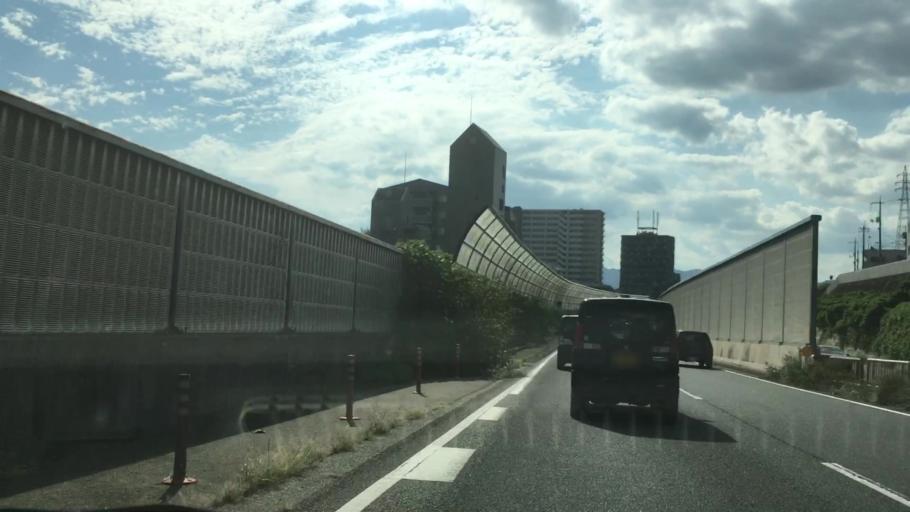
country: JP
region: Hiroshima
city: Hatsukaichi
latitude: 34.3769
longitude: 132.3839
